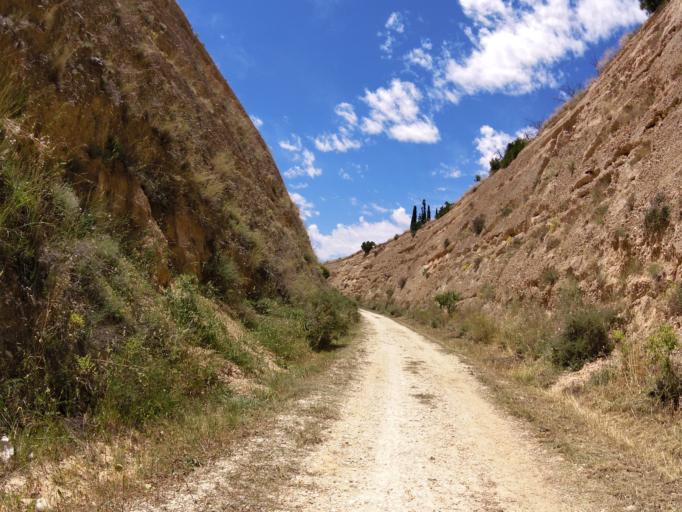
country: ES
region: Valencia
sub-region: Provincia de Alicante
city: Agost
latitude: 38.4513
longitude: -0.6722
